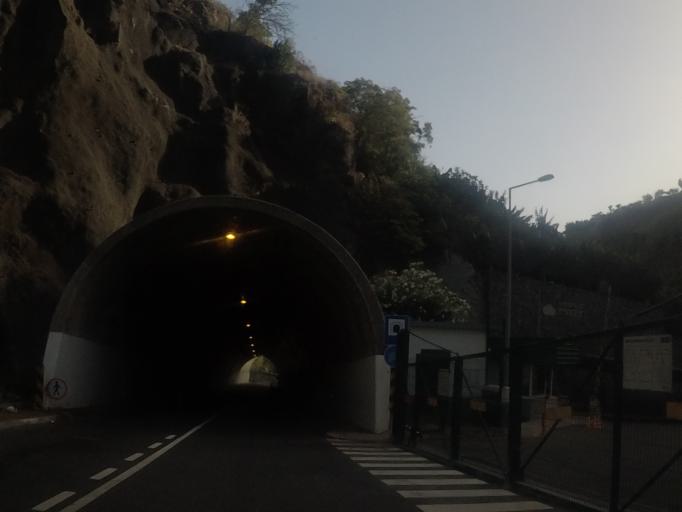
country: PT
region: Madeira
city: Ponta do Sol
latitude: 32.6869
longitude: -17.0975
